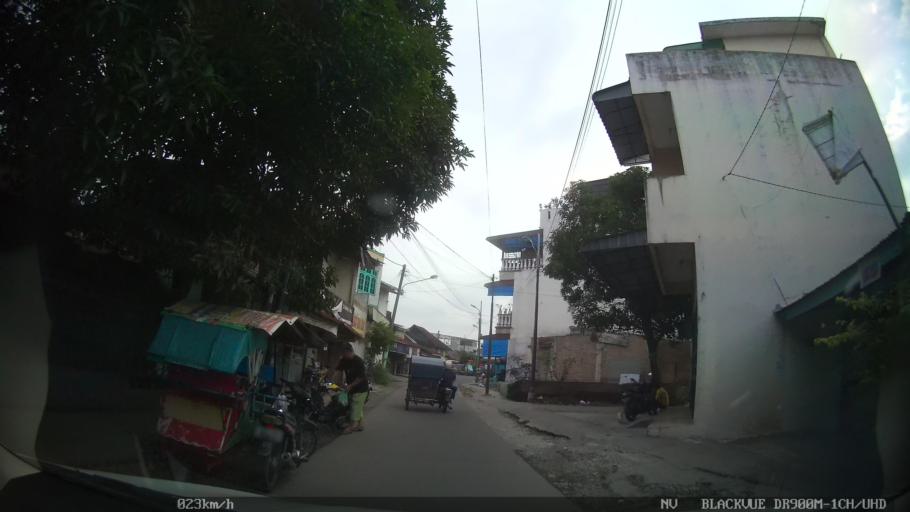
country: ID
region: North Sumatra
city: Medan
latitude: 3.6082
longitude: 98.6830
